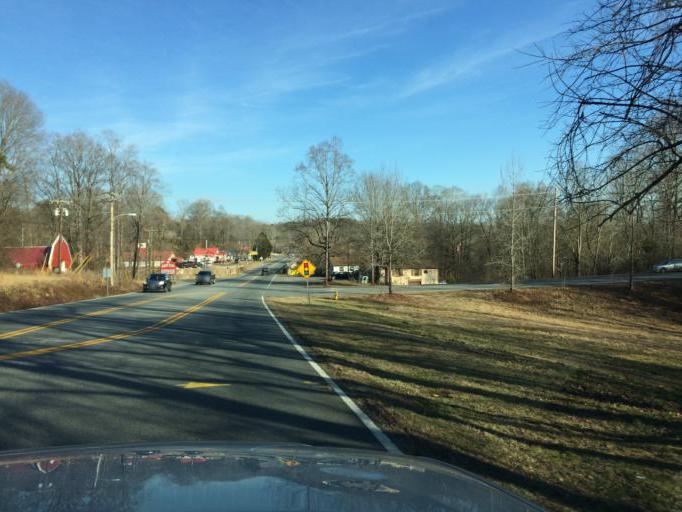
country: US
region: North Carolina
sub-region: Rutherford County
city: Forest City
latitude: 35.3339
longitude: -81.8418
